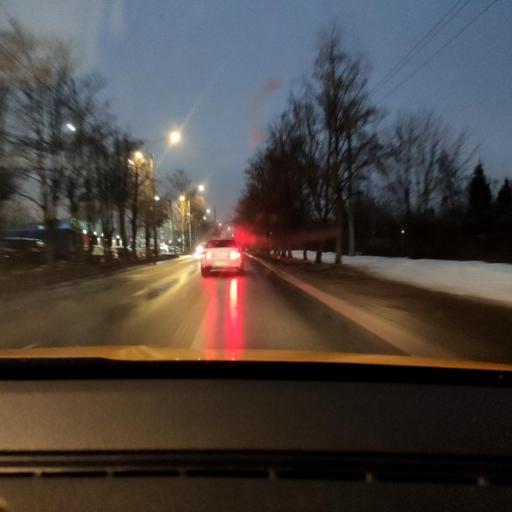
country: RU
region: Moskovskaya
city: Mosrentgen
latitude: 55.6189
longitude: 37.4564
